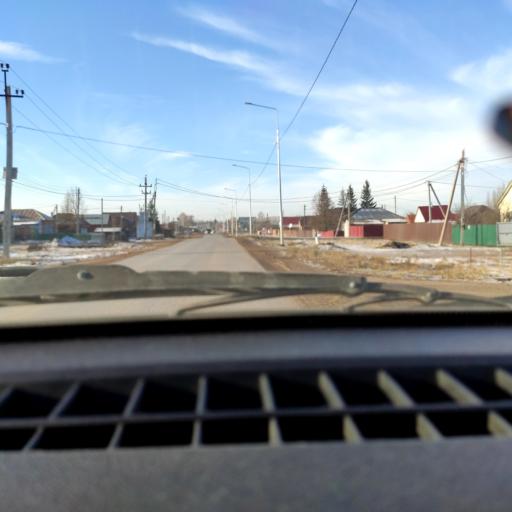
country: RU
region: Bashkortostan
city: Kabakovo
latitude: 54.5016
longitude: 55.9074
